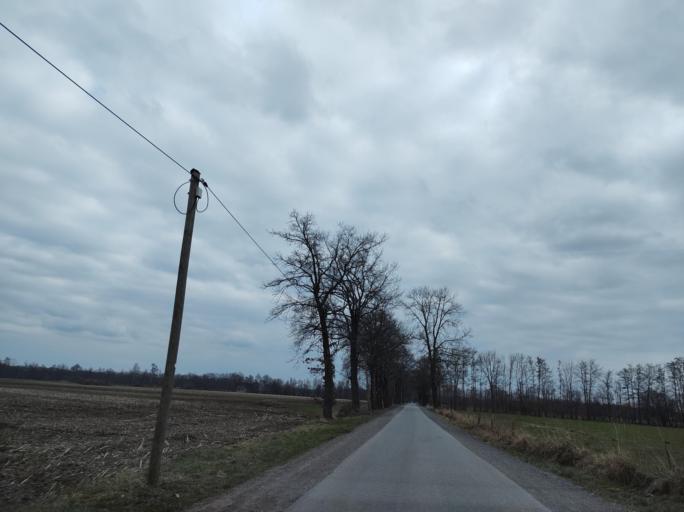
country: DE
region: North Rhine-Westphalia
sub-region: Regierungsbezirk Detmold
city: Delbruck
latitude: 51.7479
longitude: 8.5415
